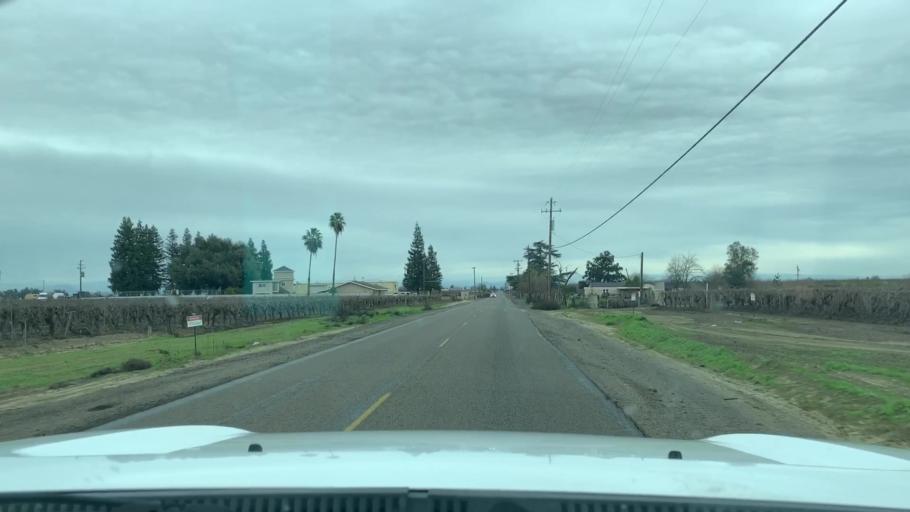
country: US
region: California
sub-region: Fresno County
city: Fowler
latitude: 36.5473
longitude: -119.7308
